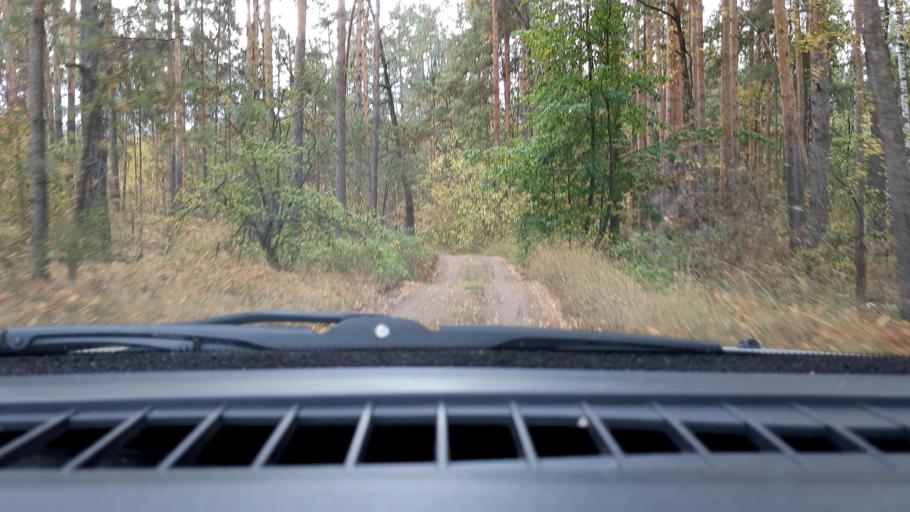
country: RU
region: Nizjnij Novgorod
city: Gorbatovka
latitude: 56.3119
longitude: 43.7197
